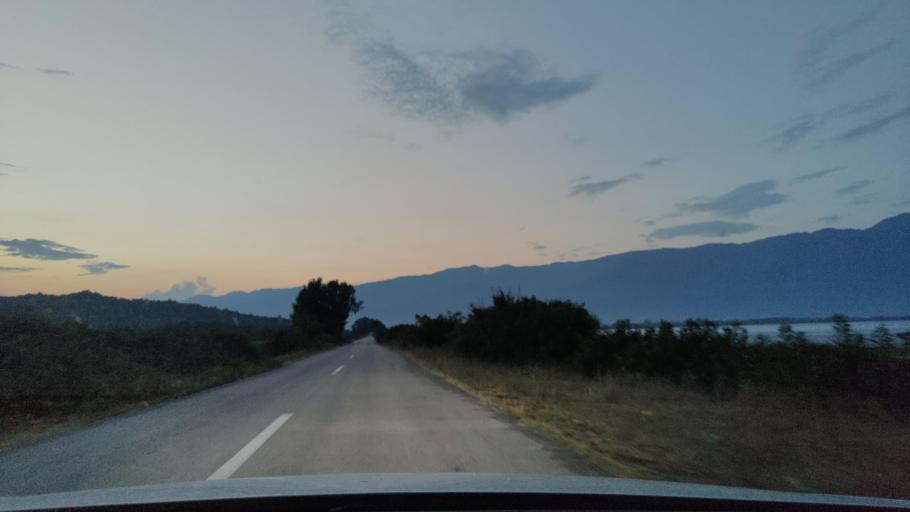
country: GR
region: Central Macedonia
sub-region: Nomos Serron
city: Chrysochorafa
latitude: 41.1886
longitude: 23.0998
